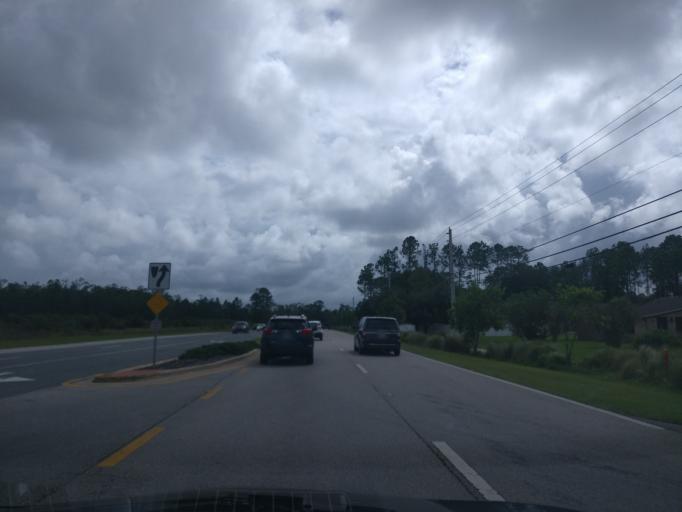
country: US
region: Florida
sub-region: Flagler County
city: Bunnell
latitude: 29.4862
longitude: -81.2215
